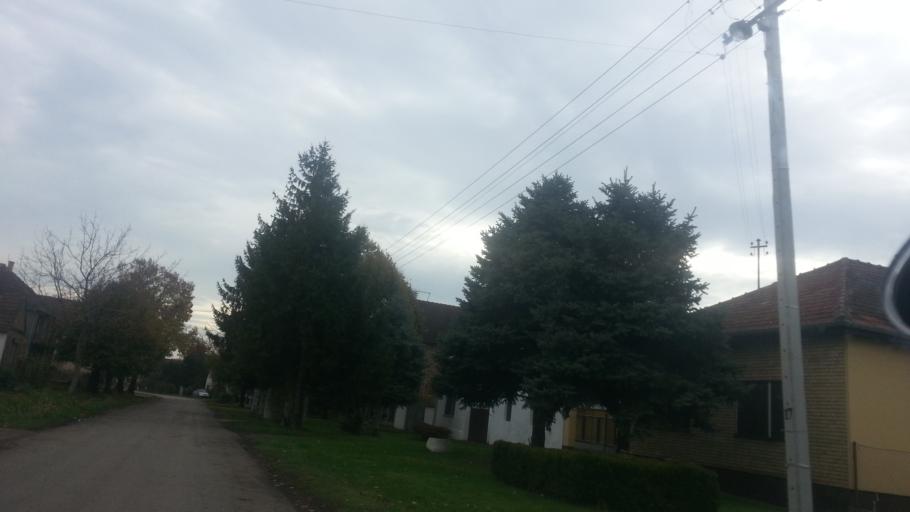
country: RS
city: Golubinci
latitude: 44.9909
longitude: 20.0579
